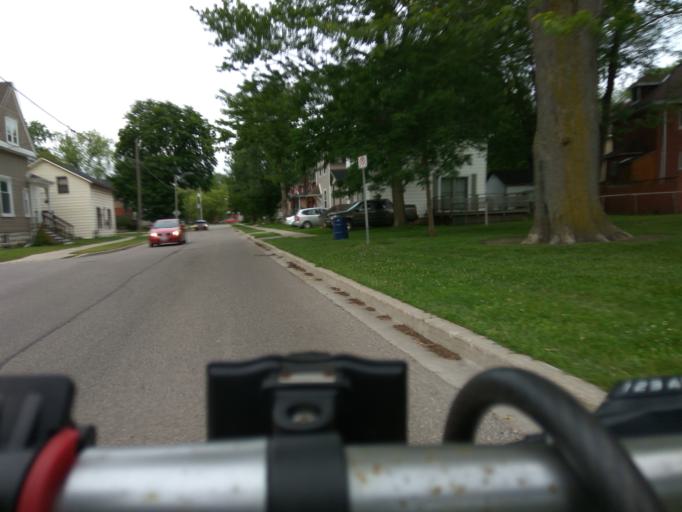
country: CA
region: Ontario
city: Stratford
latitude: 43.3630
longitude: -80.9802
